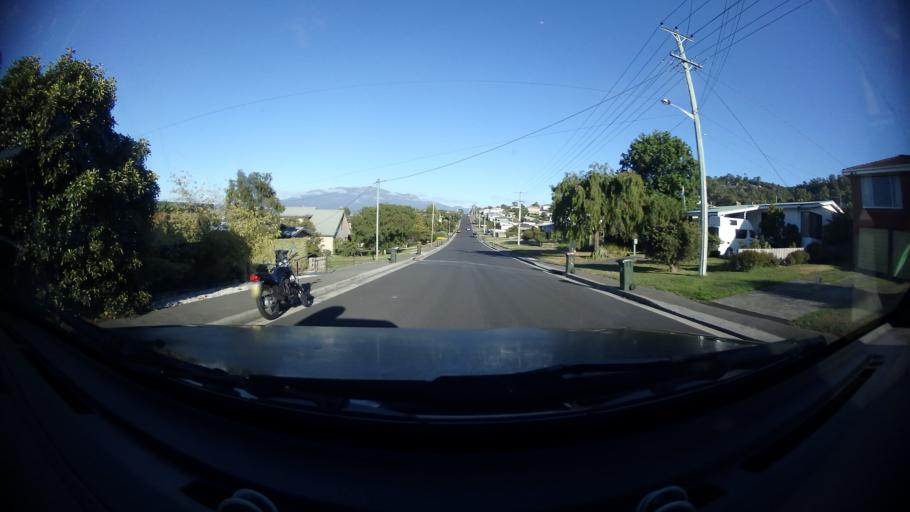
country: AU
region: Tasmania
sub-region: Clarence
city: Bellerive
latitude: -42.8740
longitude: 147.3877
